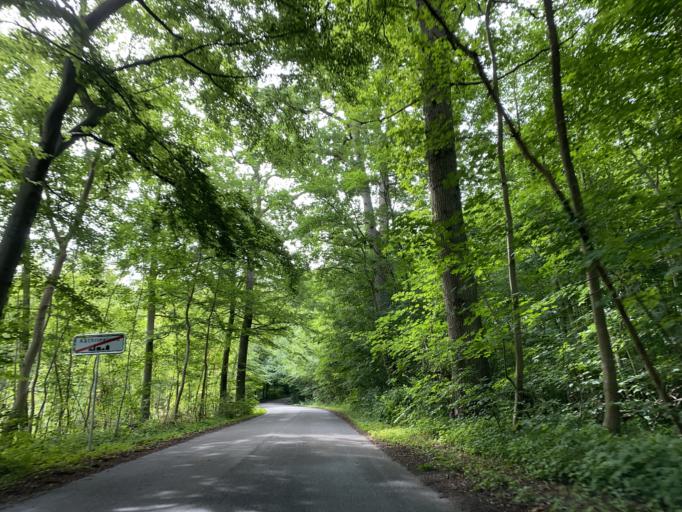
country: DK
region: South Denmark
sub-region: Sonderborg Kommune
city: Sonderborg
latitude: 54.9107
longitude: 9.8306
